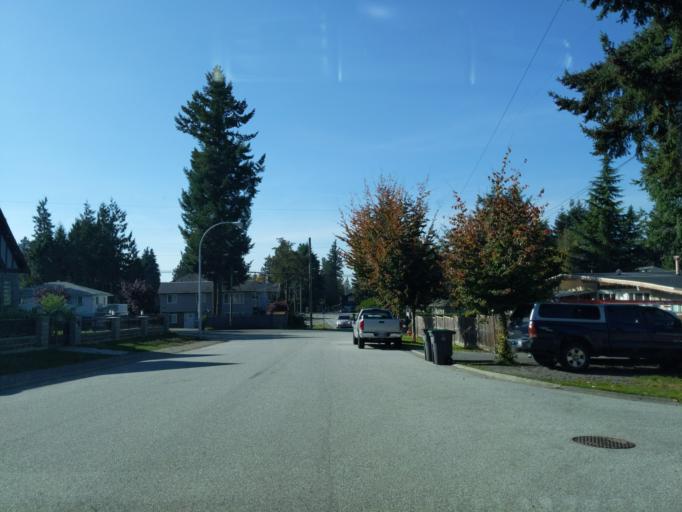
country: CA
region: British Columbia
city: New Westminster
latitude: 49.1953
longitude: -122.8655
